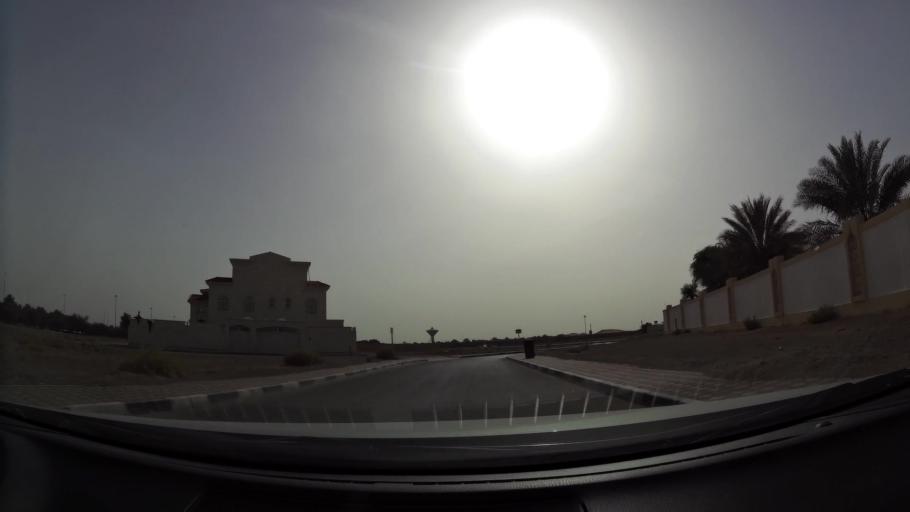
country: AE
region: Abu Dhabi
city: Al Ain
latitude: 24.1887
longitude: 55.6041
